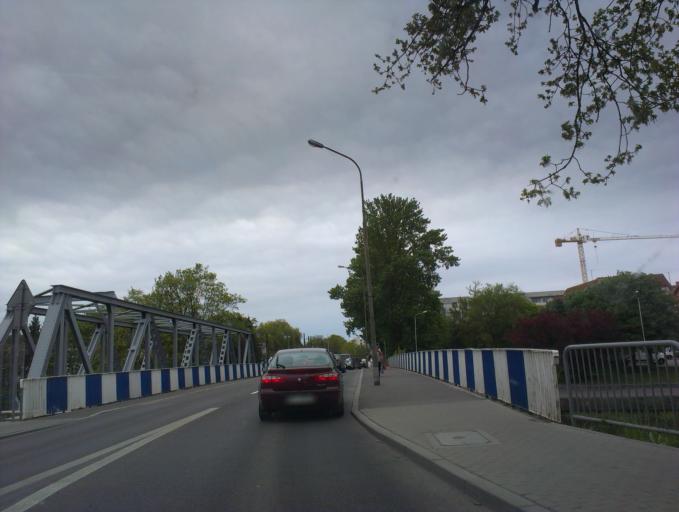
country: PL
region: West Pomeranian Voivodeship
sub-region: Powiat kolobrzeski
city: Kolobrzeg
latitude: 54.1793
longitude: 15.5633
